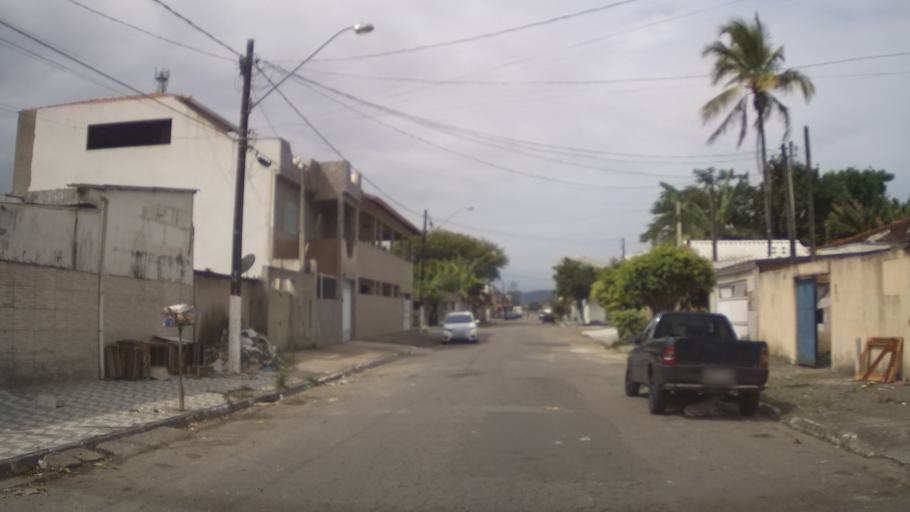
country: BR
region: Sao Paulo
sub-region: Praia Grande
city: Praia Grande
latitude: -24.0018
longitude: -46.4510
